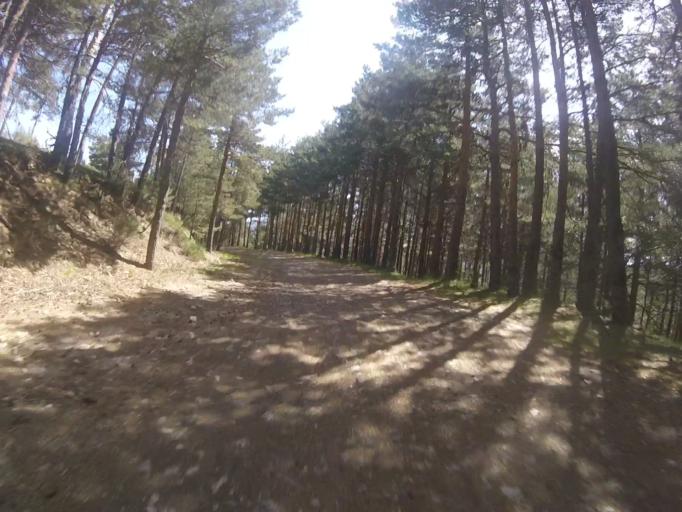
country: ES
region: Madrid
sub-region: Provincia de Madrid
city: Cercedilla
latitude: 40.8056
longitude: -4.0511
